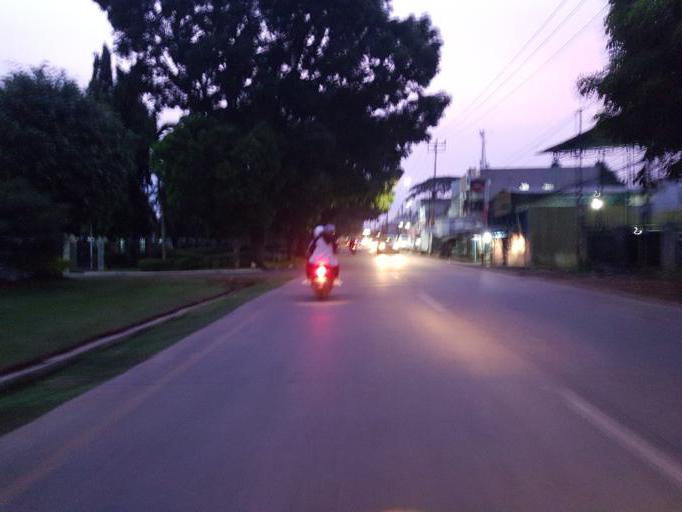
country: ID
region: West Java
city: Serpong
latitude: -6.3252
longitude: 106.6688
